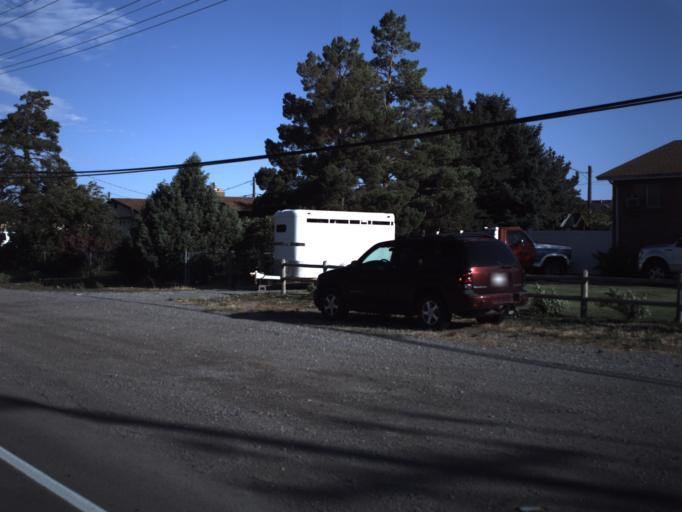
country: US
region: Utah
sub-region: Utah County
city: Spanish Fork
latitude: 40.0971
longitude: -111.6197
